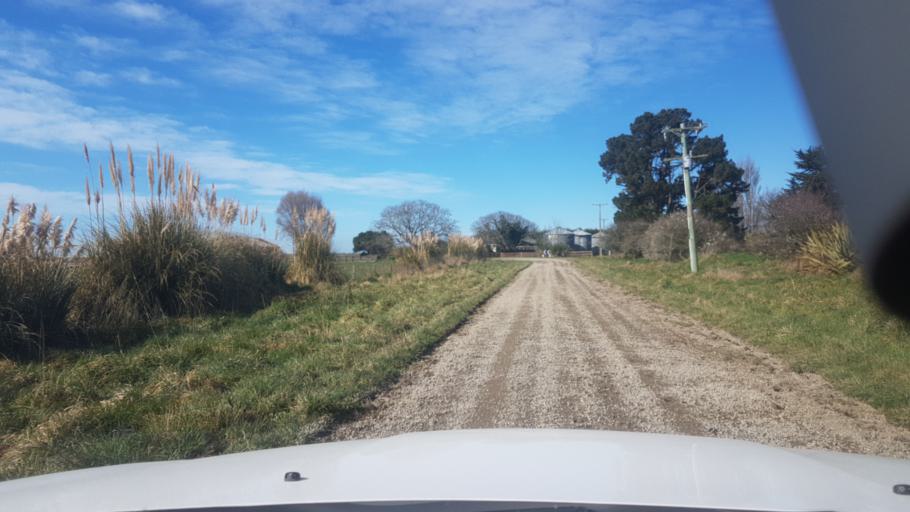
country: NZ
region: Canterbury
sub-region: Timaru District
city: Timaru
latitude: -44.2661
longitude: 171.3543
